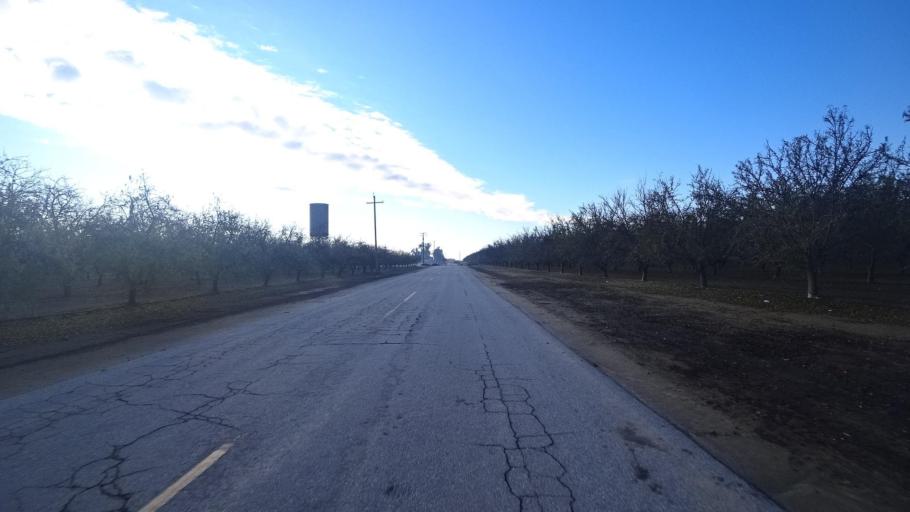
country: US
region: California
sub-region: Kern County
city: Delano
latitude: 35.7221
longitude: -119.3303
